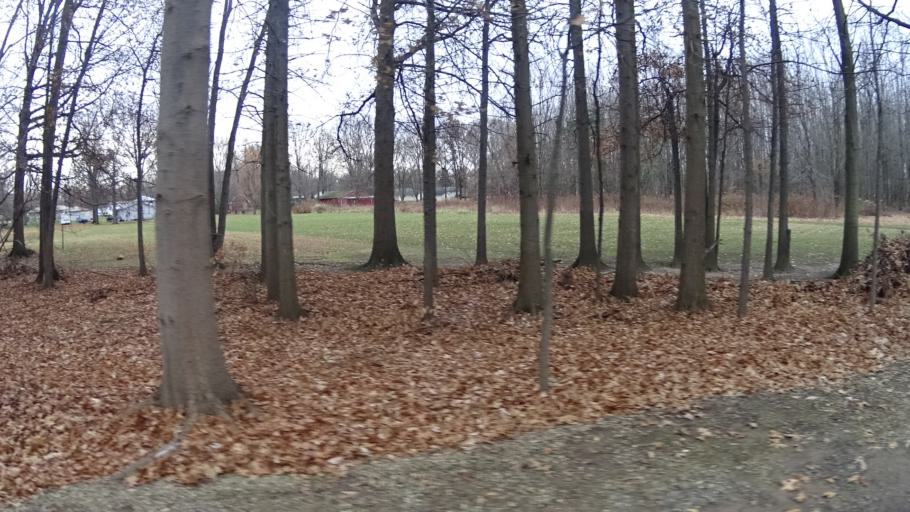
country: US
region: Ohio
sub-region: Lorain County
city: North Ridgeville
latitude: 41.3619
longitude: -82.0237
